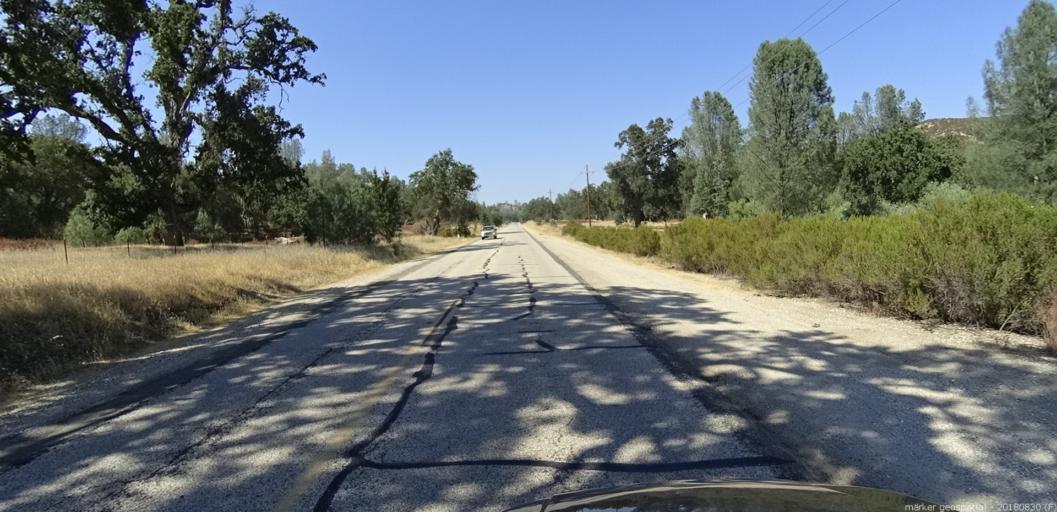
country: US
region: California
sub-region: Monterey County
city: King City
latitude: 35.9830
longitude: -121.1779
